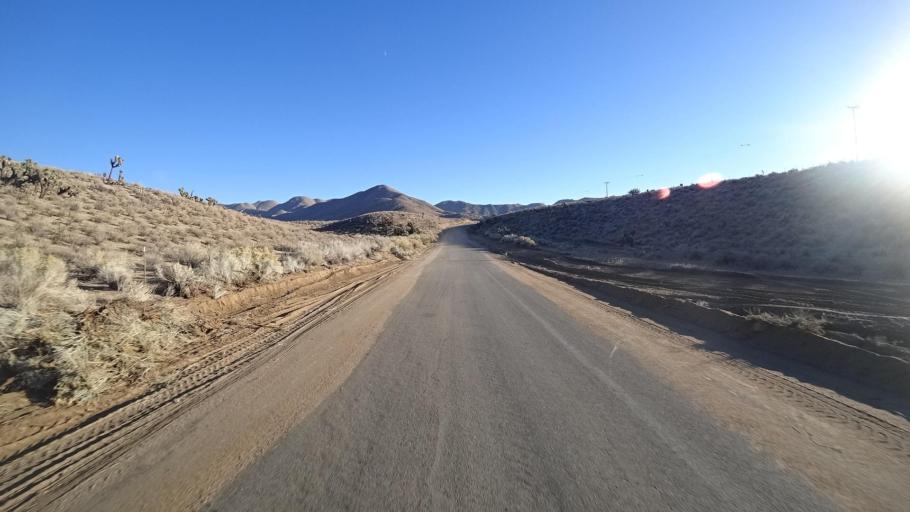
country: US
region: California
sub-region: Kern County
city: Weldon
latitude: 35.6060
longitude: -118.2434
